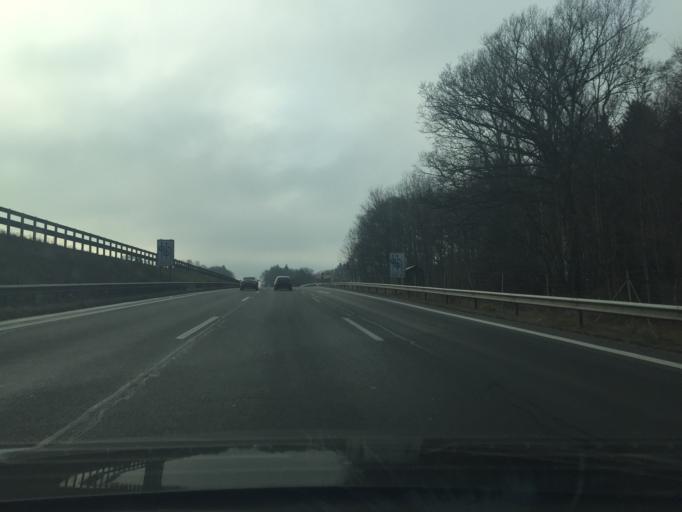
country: DE
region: Bavaria
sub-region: Upper Bavaria
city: Bernau am Chiemsee
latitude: 47.8112
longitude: 12.3478
